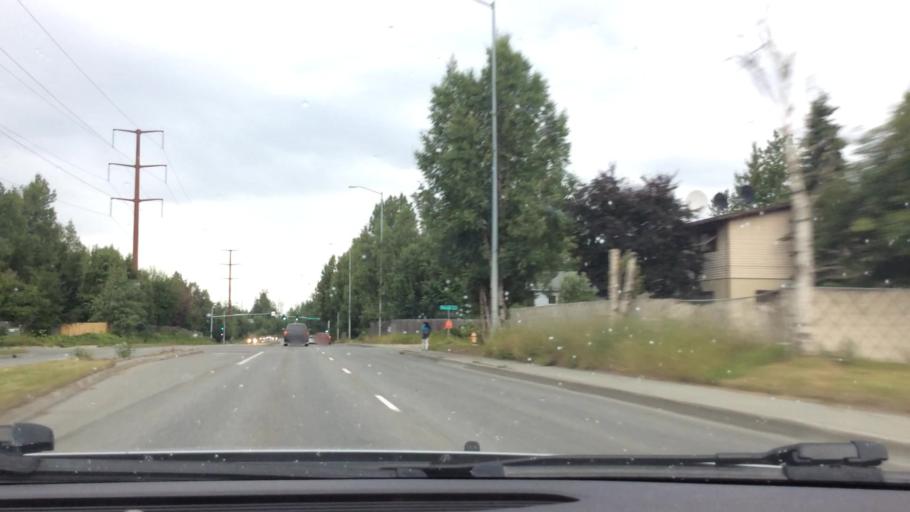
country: US
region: Alaska
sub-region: Anchorage Municipality
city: Anchorage
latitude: 61.1953
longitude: -149.7846
